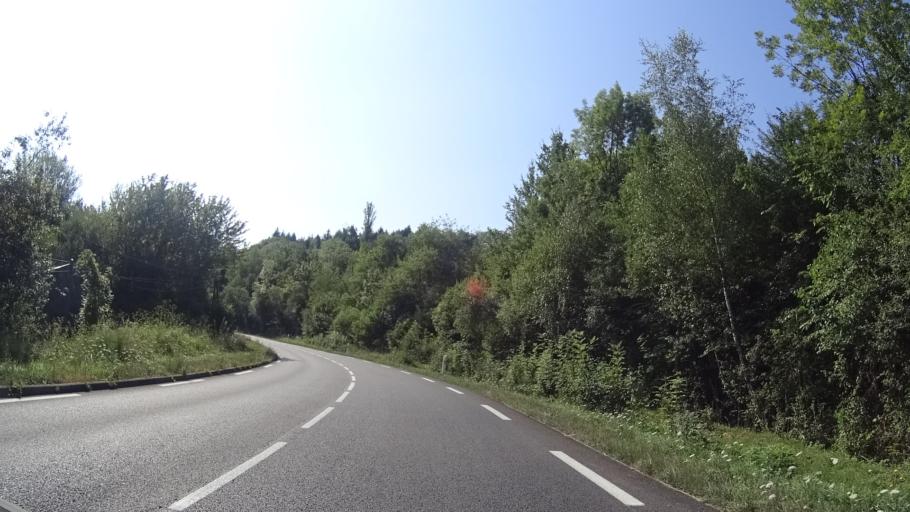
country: FR
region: Midi-Pyrenees
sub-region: Departement de l'Ariege
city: Lavelanet
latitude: 42.9211
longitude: 1.7522
